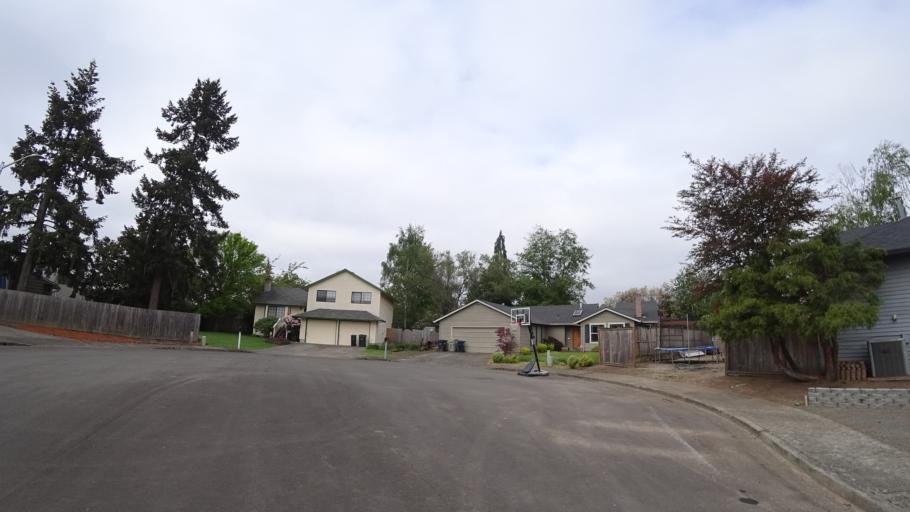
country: US
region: Oregon
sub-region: Washington County
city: Aloha
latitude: 45.5175
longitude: -122.8731
